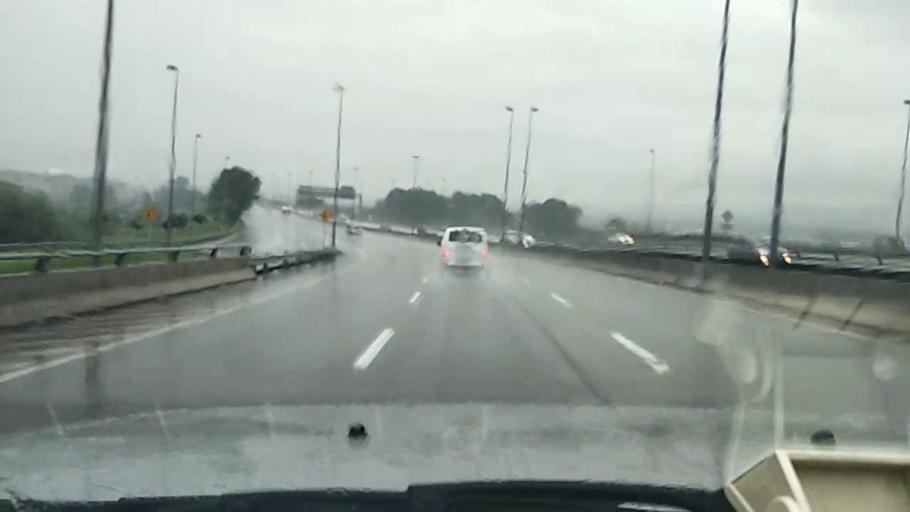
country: MY
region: Selangor
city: Kampong Baharu Balakong
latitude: 2.9933
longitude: 101.7740
